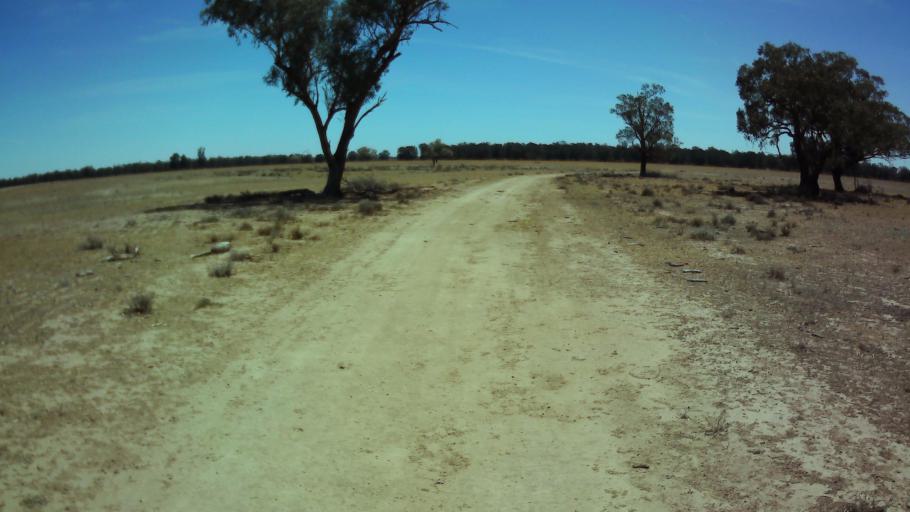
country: AU
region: New South Wales
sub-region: Bland
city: West Wyalong
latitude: -33.8381
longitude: 147.6325
